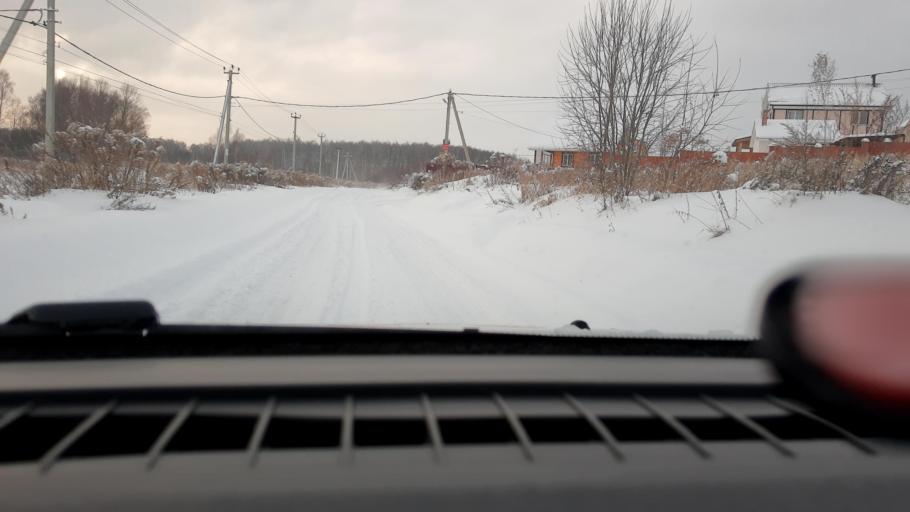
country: RU
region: Nizjnij Novgorod
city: Afonino
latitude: 56.1285
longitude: 44.0005
